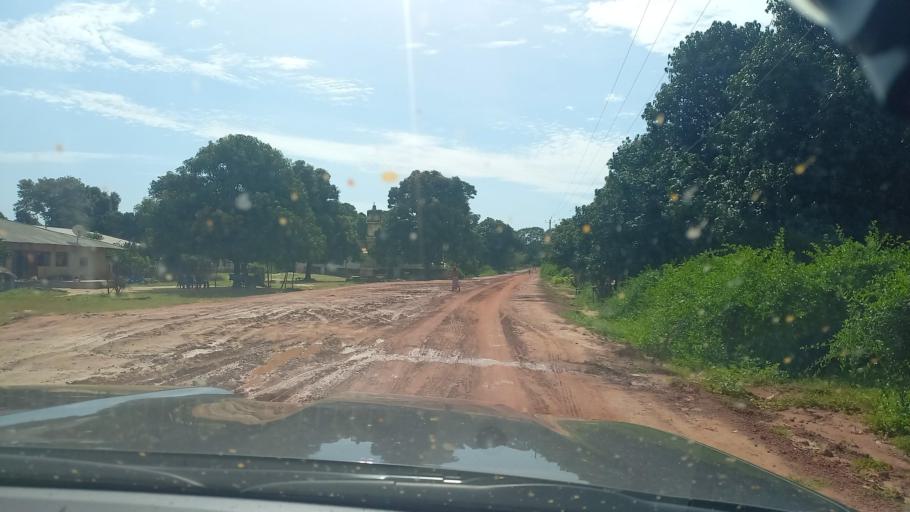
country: SN
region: Ziguinchor
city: Ziguinchor
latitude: 12.6747
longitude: -16.1939
